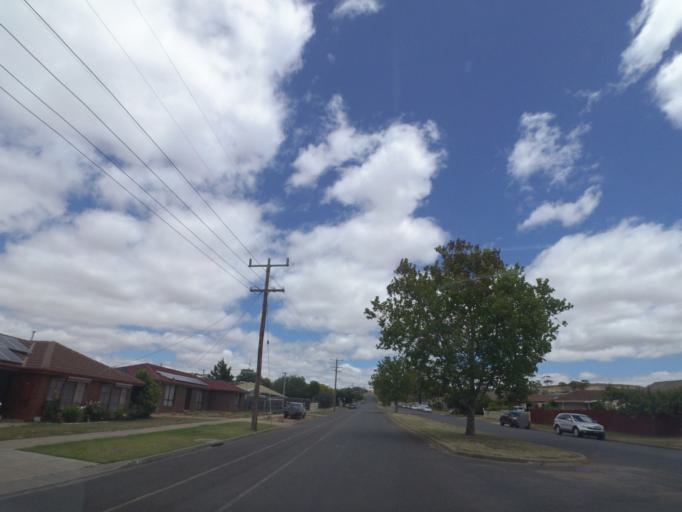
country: AU
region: Victoria
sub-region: Moorabool
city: Bacchus Marsh
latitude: -37.6584
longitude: 144.4348
